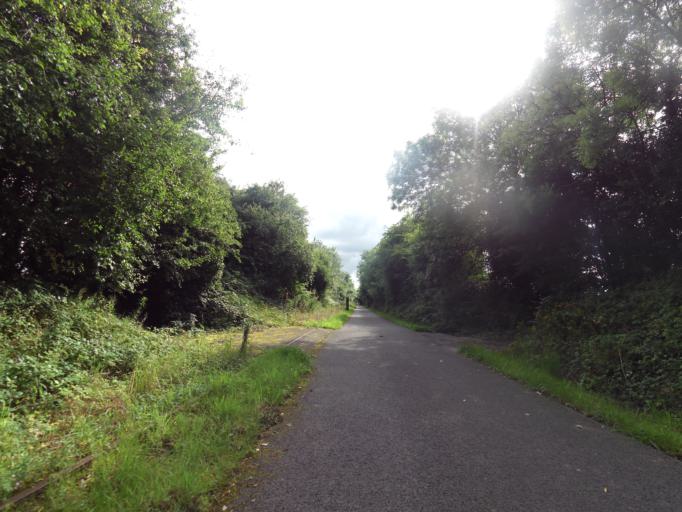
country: IE
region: Leinster
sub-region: An Iarmhi
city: An Muileann gCearr
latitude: 53.5002
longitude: -7.4361
